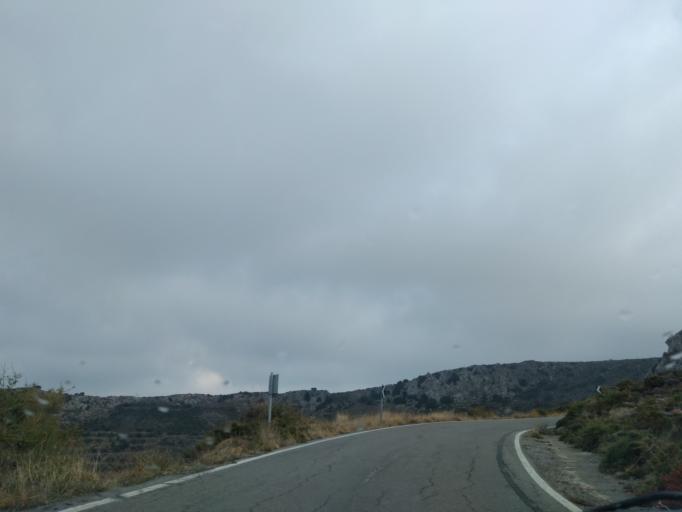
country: GR
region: Crete
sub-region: Nomos Lasithiou
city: Siteia
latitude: 35.1548
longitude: 26.0190
